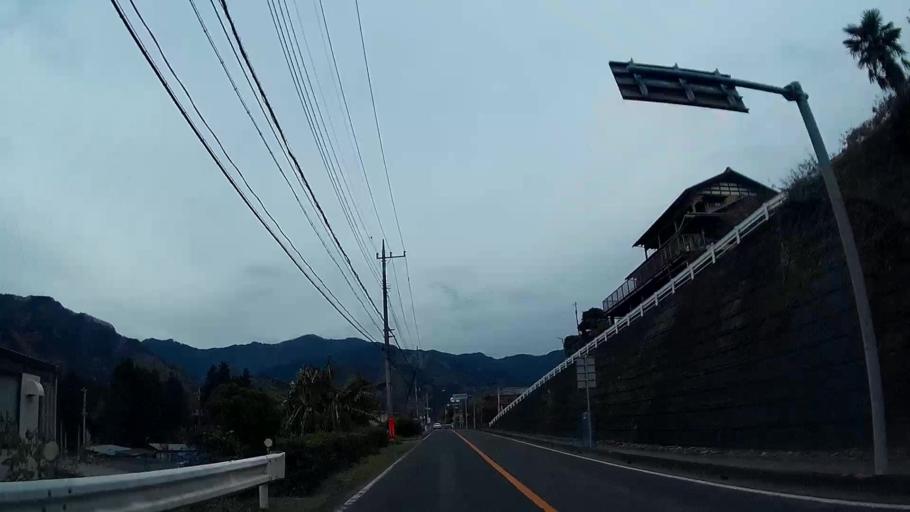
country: JP
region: Saitama
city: Chichibu
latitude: 35.9617
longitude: 138.9944
